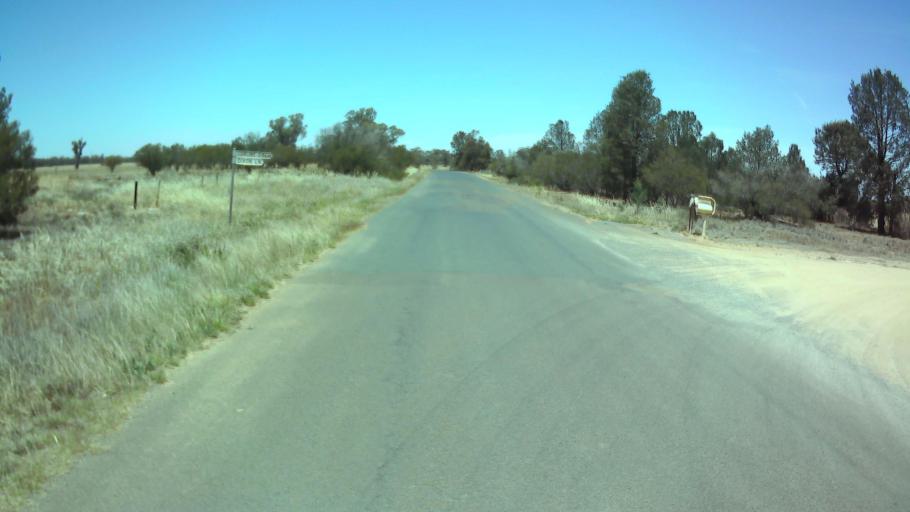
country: AU
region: New South Wales
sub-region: Weddin
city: Grenfell
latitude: -34.0574
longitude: 147.7802
